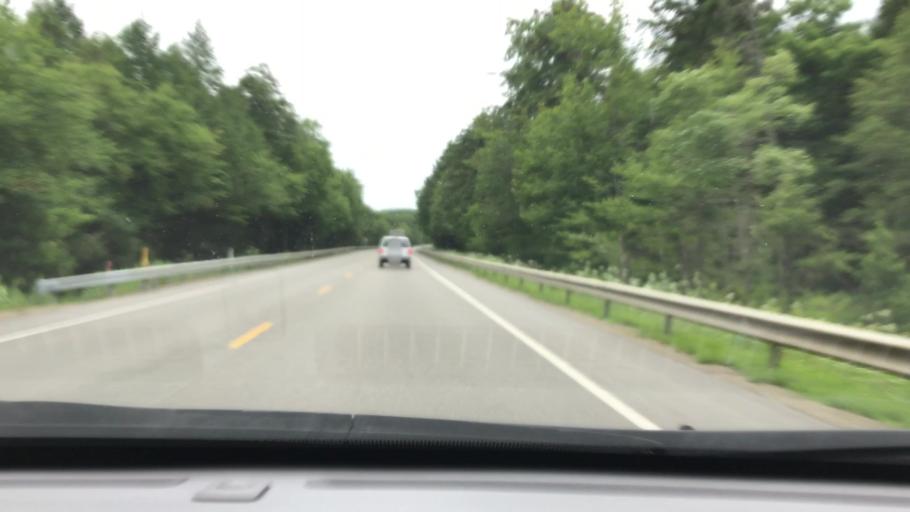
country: US
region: Pennsylvania
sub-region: McKean County
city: Kane
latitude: 41.6829
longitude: -78.6879
